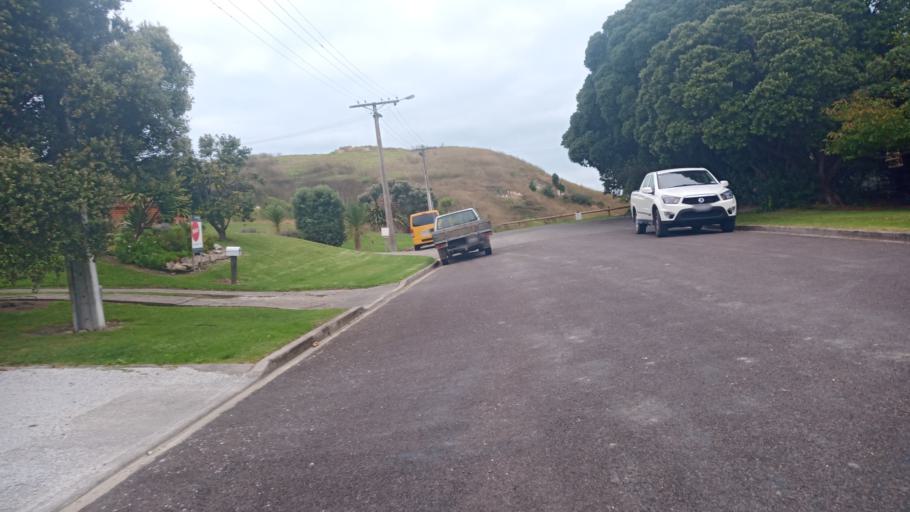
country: NZ
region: Gisborne
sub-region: Gisborne District
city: Gisborne
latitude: -38.6845
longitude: 178.0425
